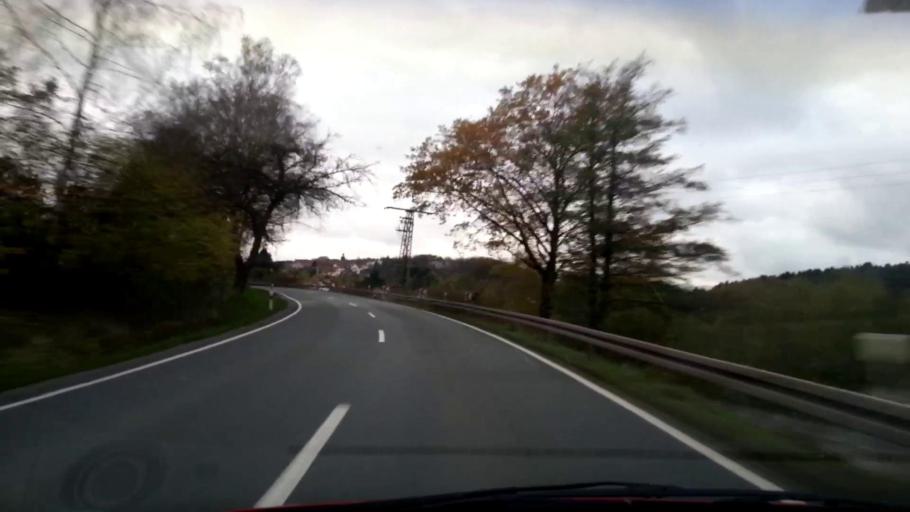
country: DE
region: Bavaria
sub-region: Upper Franconia
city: Kueps Oberfranken
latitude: 50.2127
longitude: 11.2878
